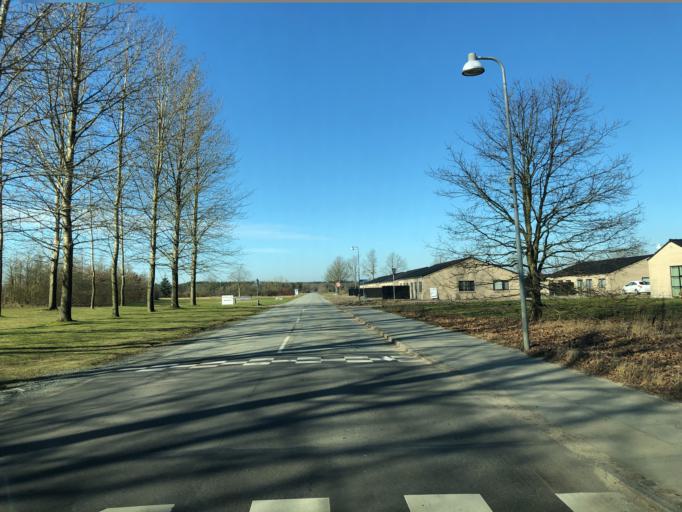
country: DK
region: Central Jutland
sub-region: Ikast-Brande Kommune
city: Bording Kirkeby
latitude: 56.1499
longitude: 9.2718
